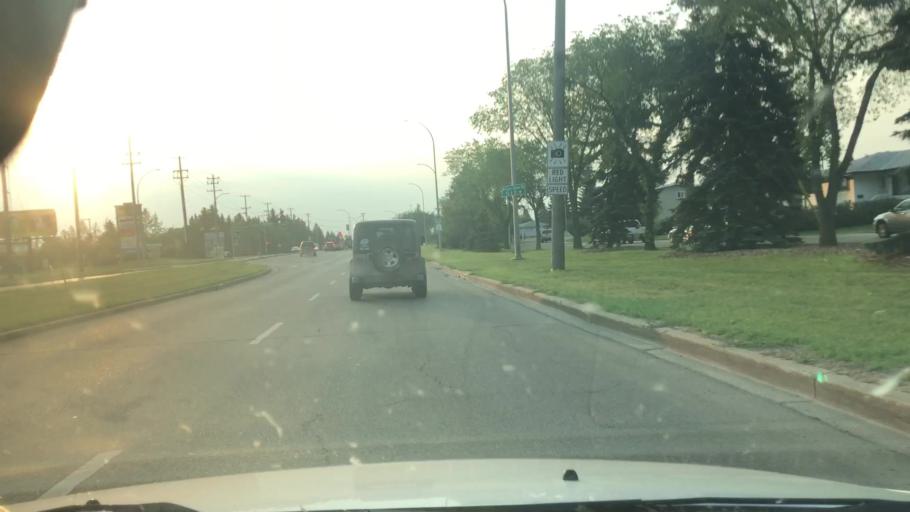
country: CA
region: Alberta
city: Edmonton
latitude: 53.5994
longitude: -113.5198
